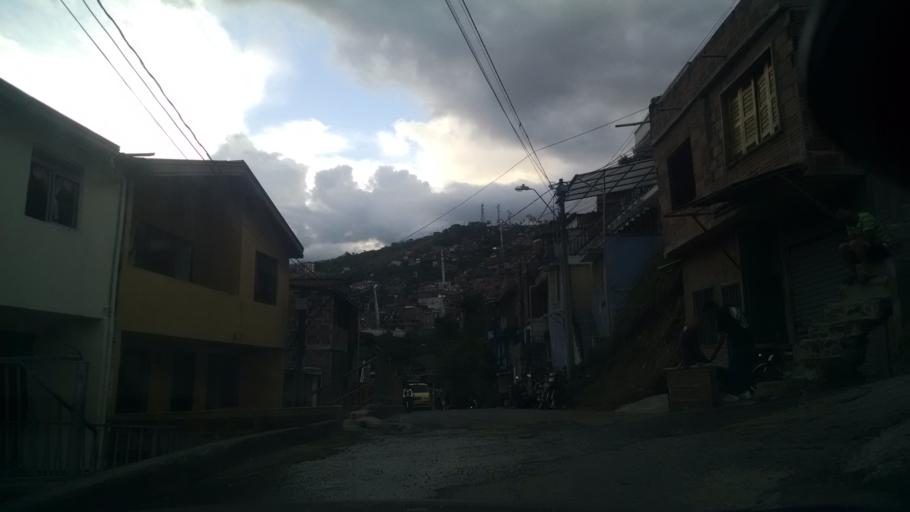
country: CO
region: Antioquia
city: Medellin
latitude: 6.2638
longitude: -75.6125
